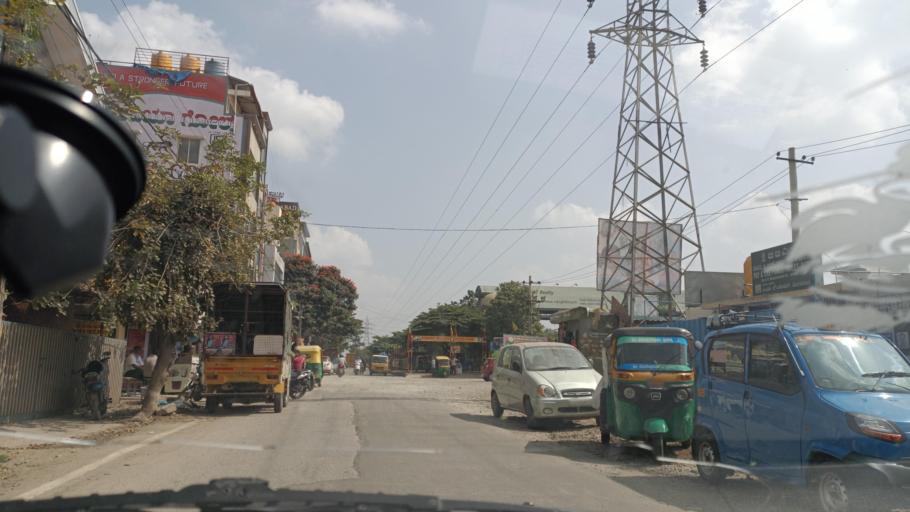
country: IN
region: Karnataka
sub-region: Bangalore Urban
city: Bangalore
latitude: 13.0230
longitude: 77.6472
